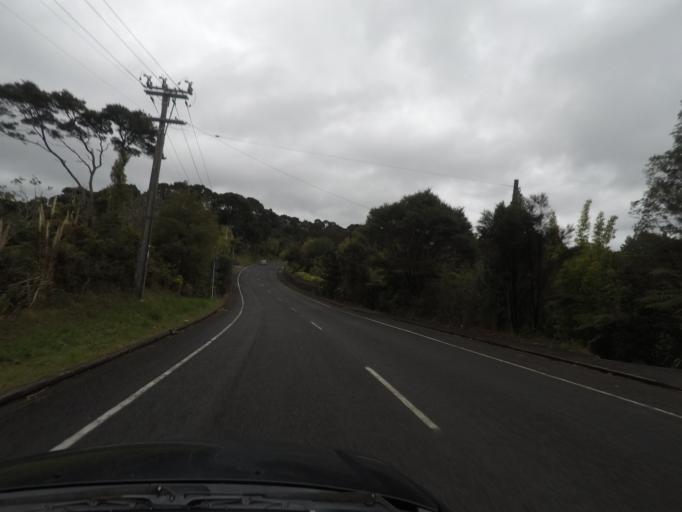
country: NZ
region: Auckland
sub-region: Auckland
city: Titirangi
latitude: -36.9262
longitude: 174.5980
